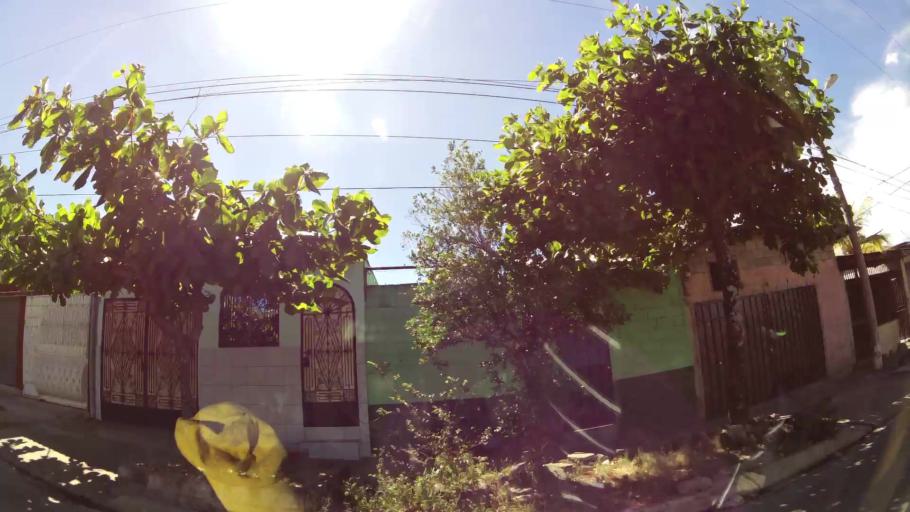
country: SV
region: San Salvador
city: Apopa
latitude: 13.8145
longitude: -89.1753
